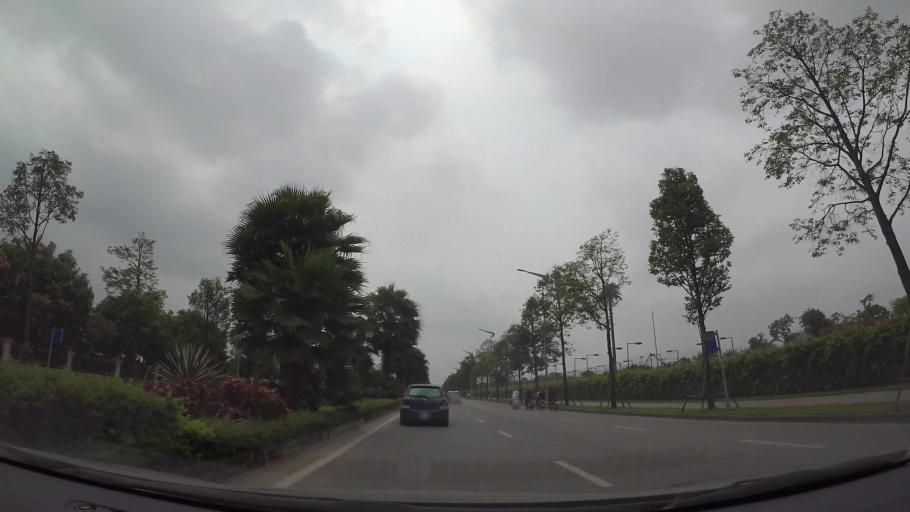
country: VN
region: Ha Noi
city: Trau Quy
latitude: 21.0501
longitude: 105.9083
